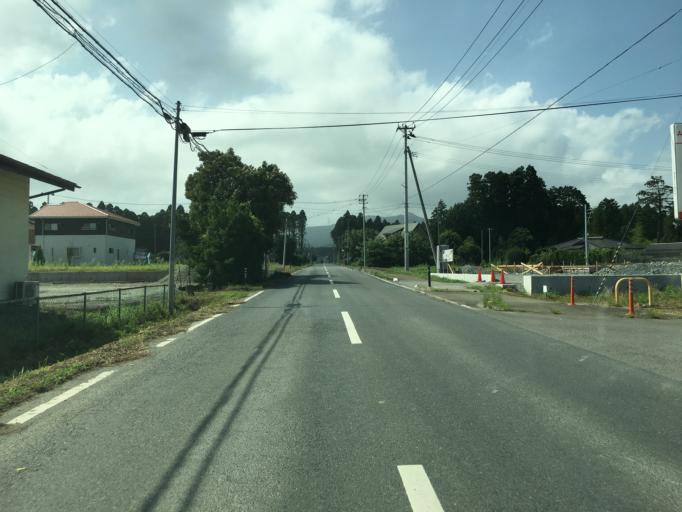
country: JP
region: Miyagi
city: Marumori
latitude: 37.8383
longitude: 140.9013
